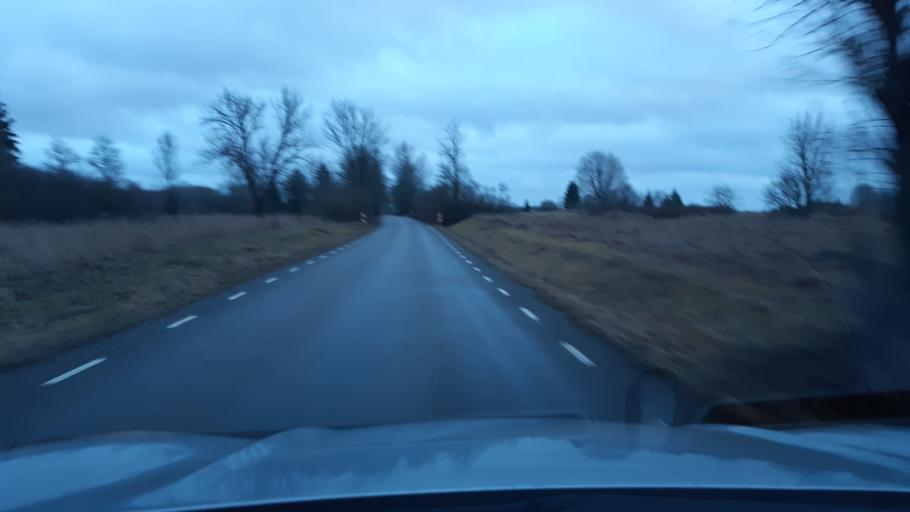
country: EE
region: Raplamaa
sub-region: Rapla vald
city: Rapla
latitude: 58.9923
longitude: 24.7240
